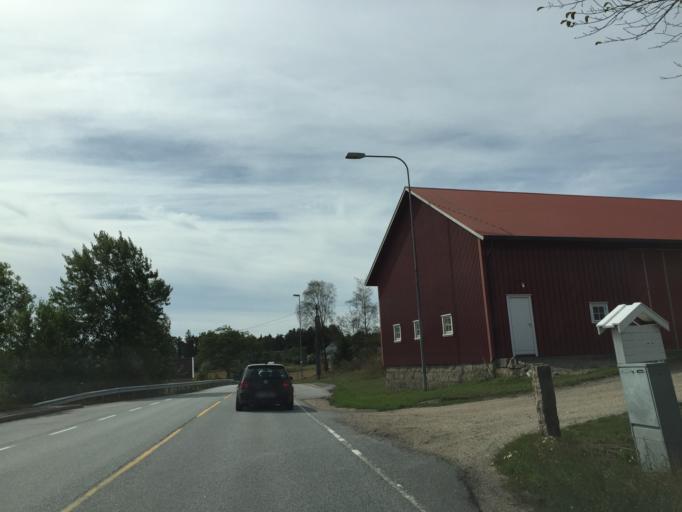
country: NO
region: Ostfold
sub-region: Fredrikstad
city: Fredrikstad
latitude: 59.2777
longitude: 10.9015
